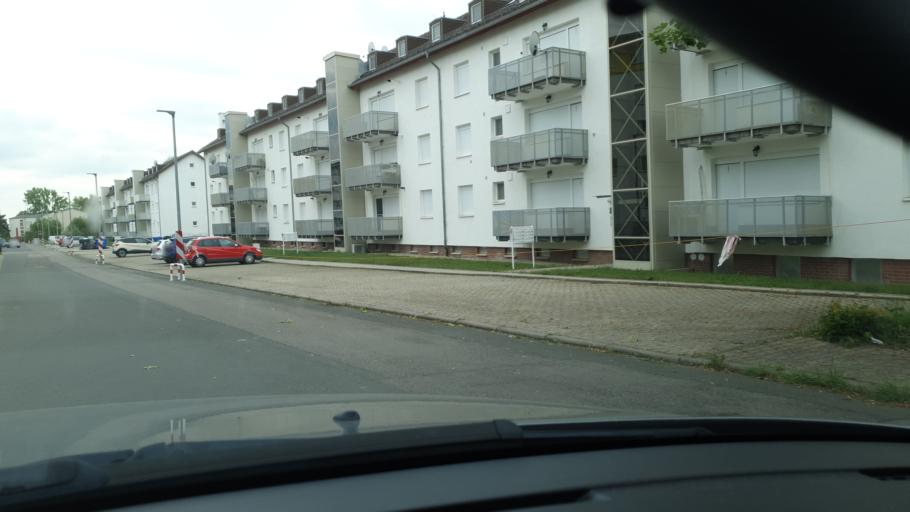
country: DE
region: Rheinland-Pfalz
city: Zweibrucken
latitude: 49.2602
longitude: 7.3579
